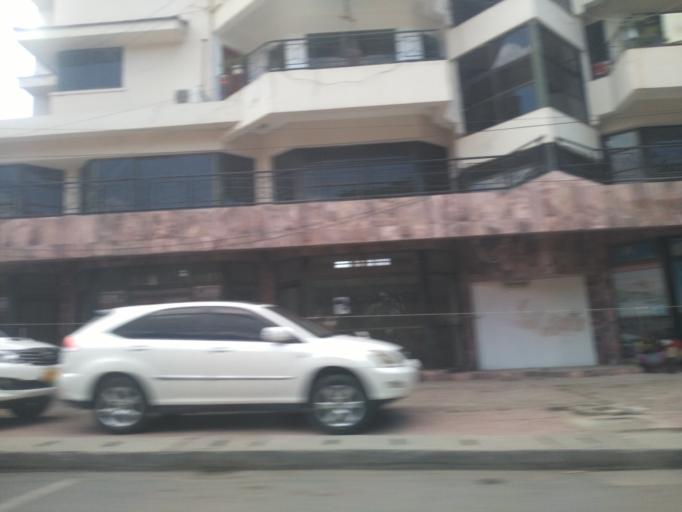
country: TZ
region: Mwanza
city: Mwanza
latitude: -2.5166
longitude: 32.9013
